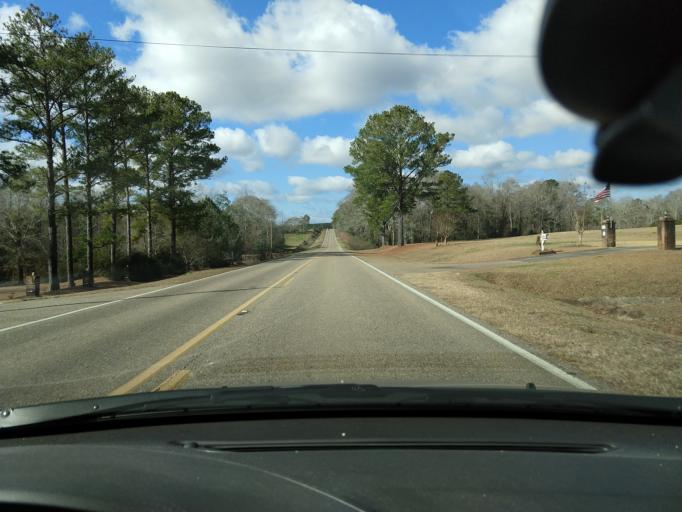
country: US
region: Alabama
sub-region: Coffee County
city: Elba
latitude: 31.3116
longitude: -86.0218
